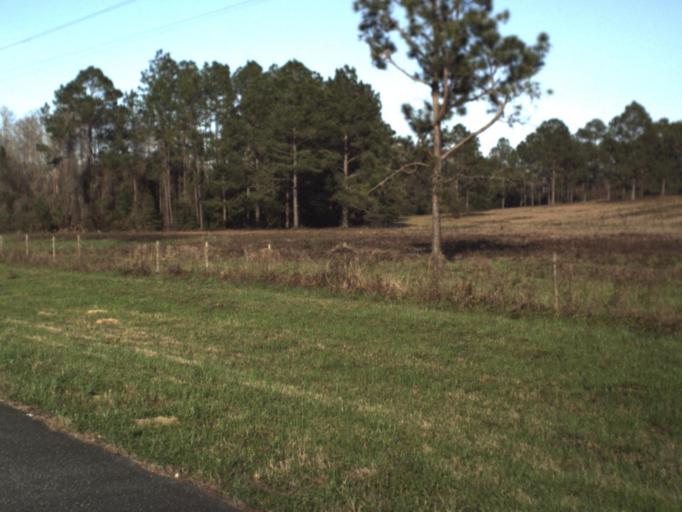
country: US
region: Florida
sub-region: Calhoun County
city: Blountstown
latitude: 30.5405
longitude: -85.1905
